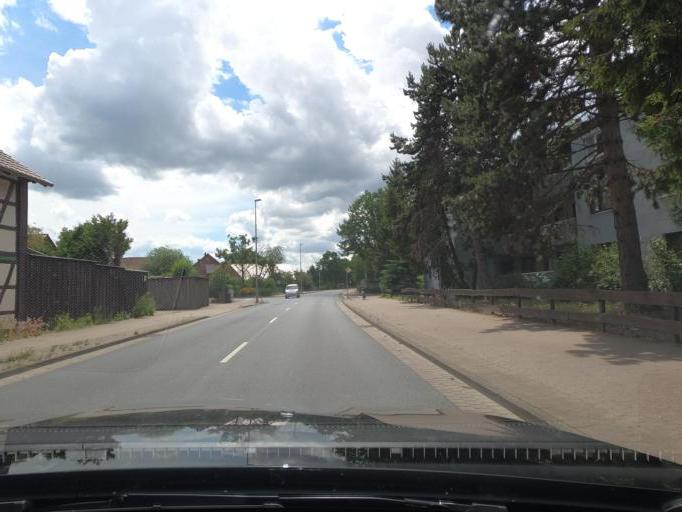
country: DE
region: Lower Saxony
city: Sehnde
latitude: 52.3108
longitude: 9.9642
